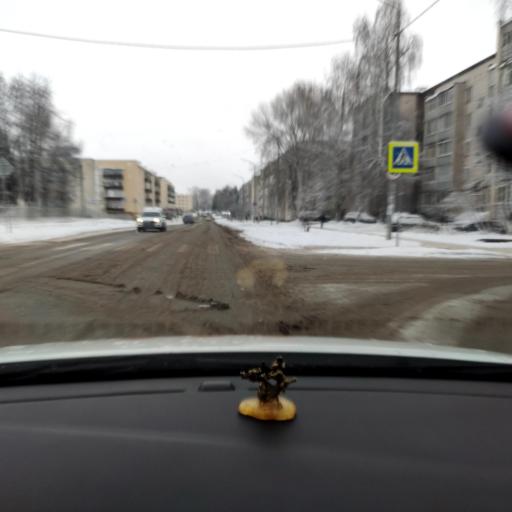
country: RU
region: Tatarstan
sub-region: Zelenodol'skiy Rayon
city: Zelenodolsk
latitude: 55.8497
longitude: 48.5182
